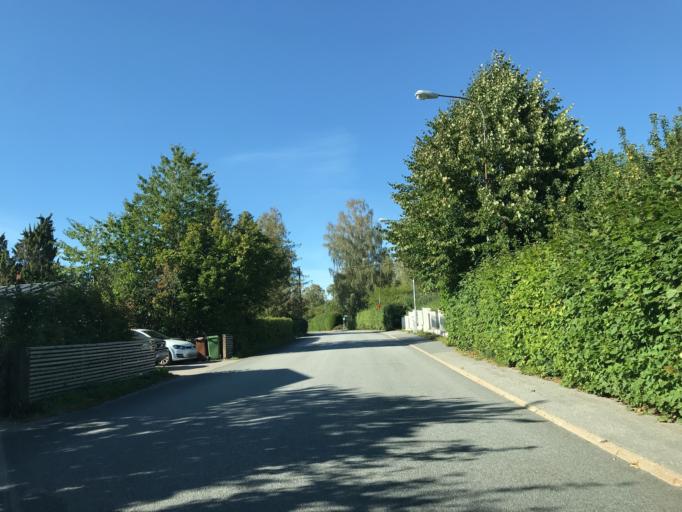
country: SE
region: Stockholm
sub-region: Sollentuna Kommun
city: Sollentuna
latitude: 59.4154
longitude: 17.9819
